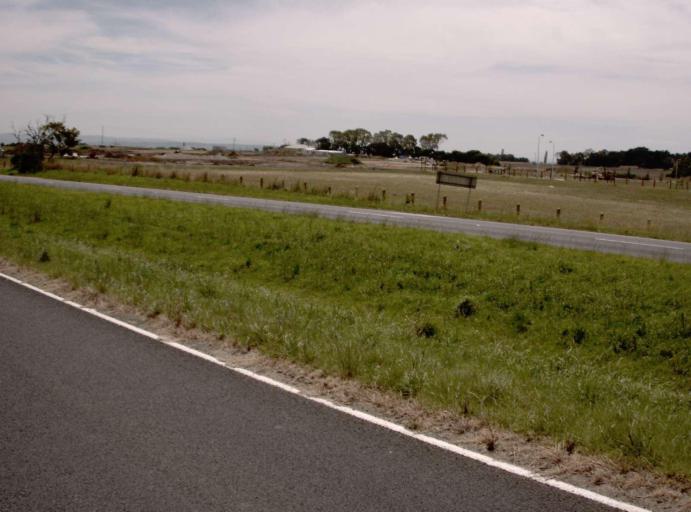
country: AU
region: Victoria
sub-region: Frankston
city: Skye
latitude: -38.1115
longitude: 145.2325
